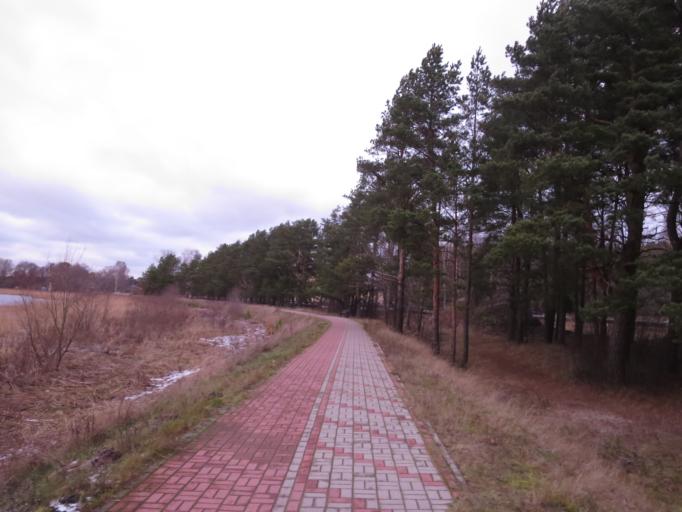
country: LV
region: Riga
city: Bergi
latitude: 56.9762
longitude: 24.3061
